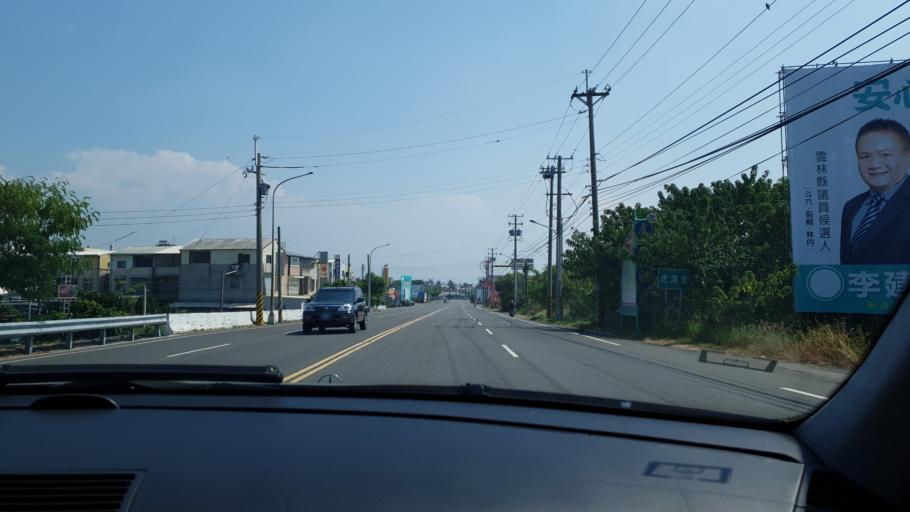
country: TW
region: Taiwan
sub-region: Yunlin
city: Douliu
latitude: 23.7296
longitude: 120.5209
